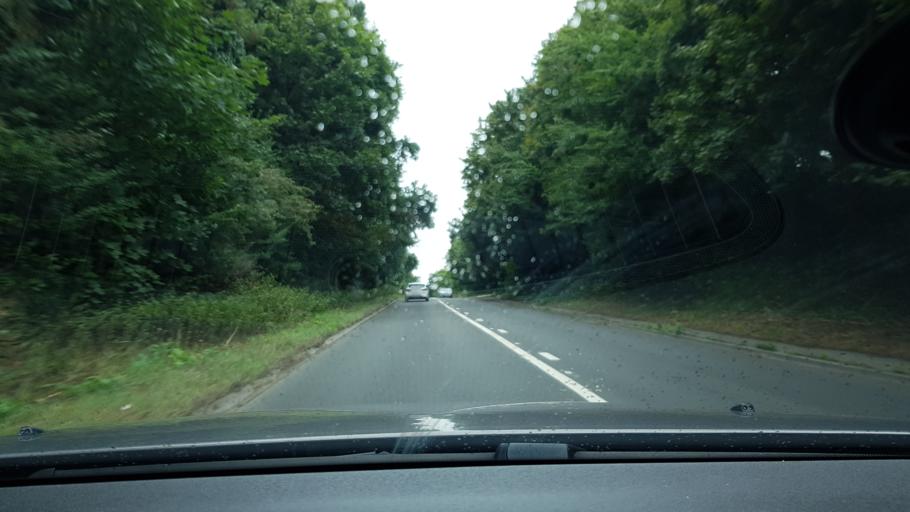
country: GB
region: England
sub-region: Wiltshire
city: Bremhill
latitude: 51.4372
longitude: -2.0326
